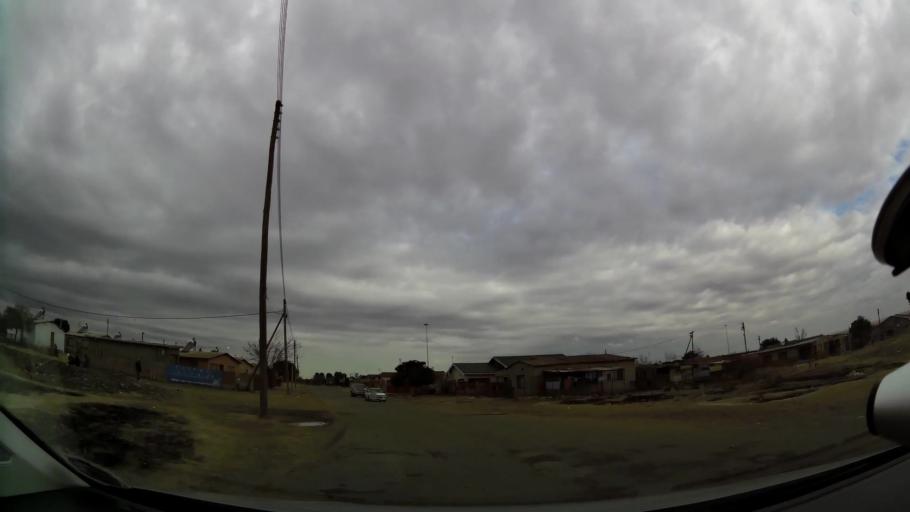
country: ZA
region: Orange Free State
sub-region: Fezile Dabi District Municipality
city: Kroonstad
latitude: -27.6461
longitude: 27.1812
